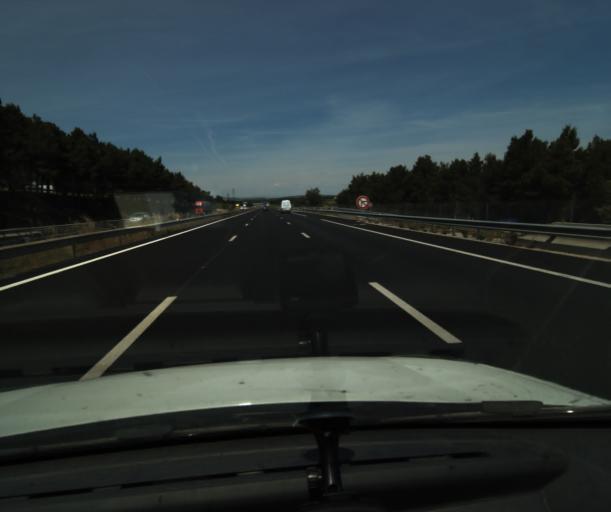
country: FR
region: Languedoc-Roussillon
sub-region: Departement de l'Aude
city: Sigean
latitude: 43.0227
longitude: 2.9523
